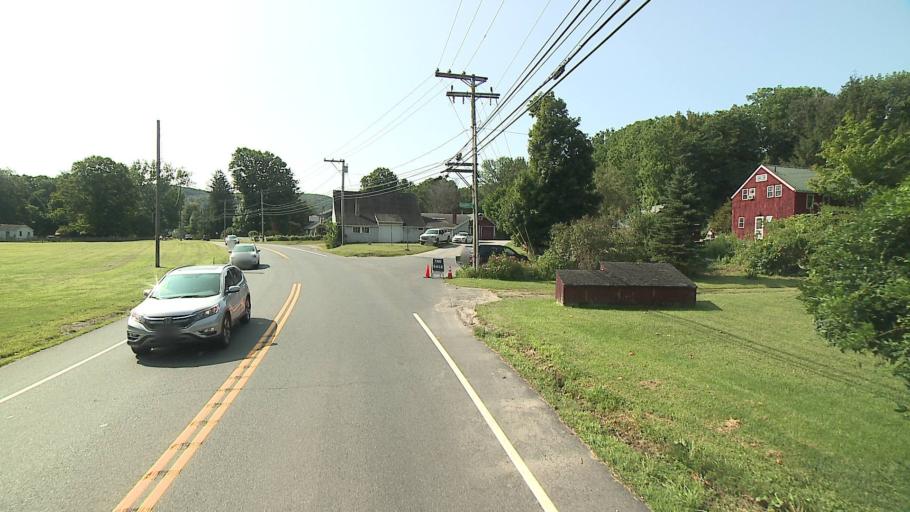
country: US
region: Connecticut
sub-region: Fairfield County
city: Sherman
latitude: 41.6426
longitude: -73.4843
